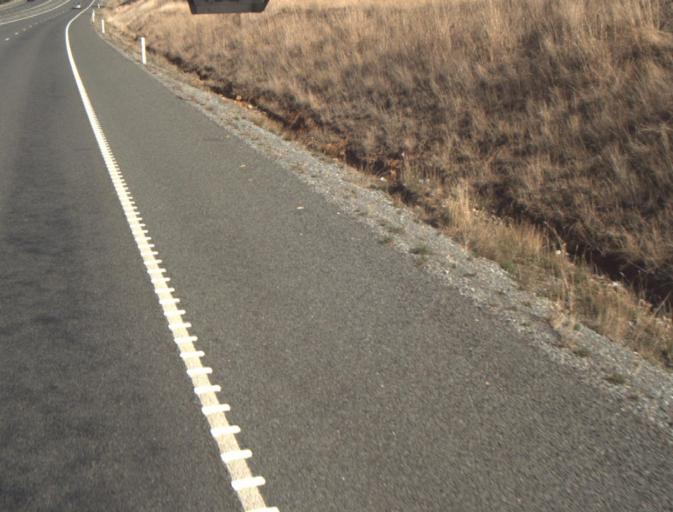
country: AU
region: Tasmania
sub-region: Launceston
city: Mayfield
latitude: -41.3582
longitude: 147.1059
